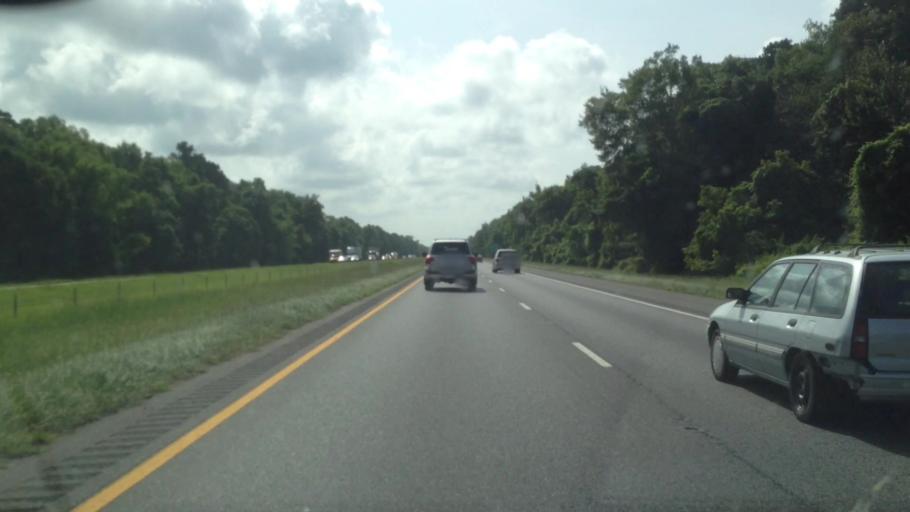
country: US
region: Louisiana
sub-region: Ascension Parish
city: Sorrento
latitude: 30.1626
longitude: -90.8446
